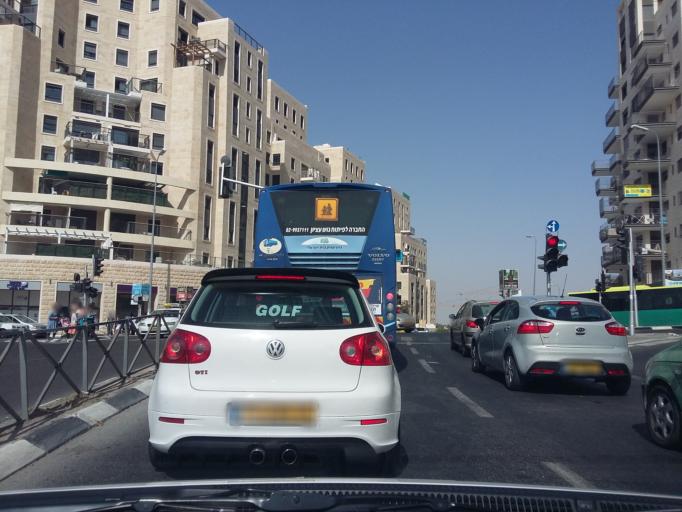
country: IL
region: Jerusalem
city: West Jerusalem
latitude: 31.7924
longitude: 35.2082
